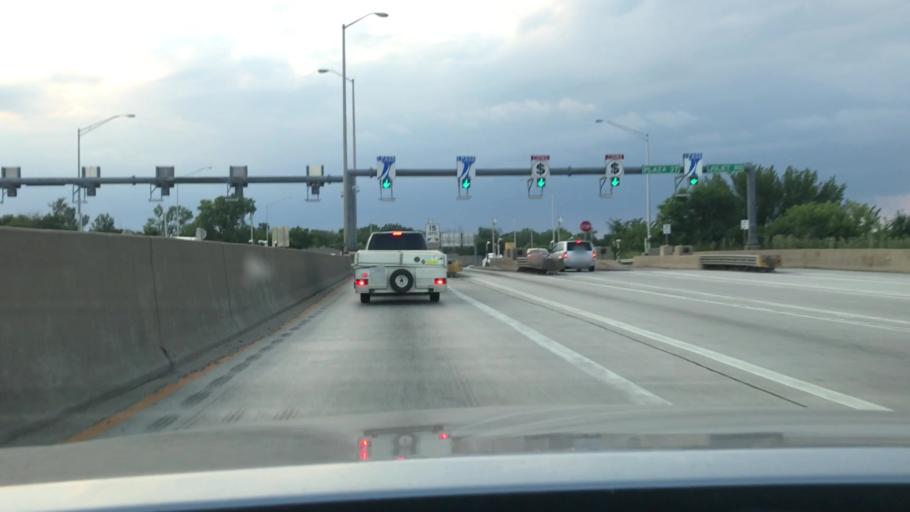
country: US
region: Illinois
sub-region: Cook County
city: Indian Head Park
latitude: 41.7647
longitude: -87.9066
